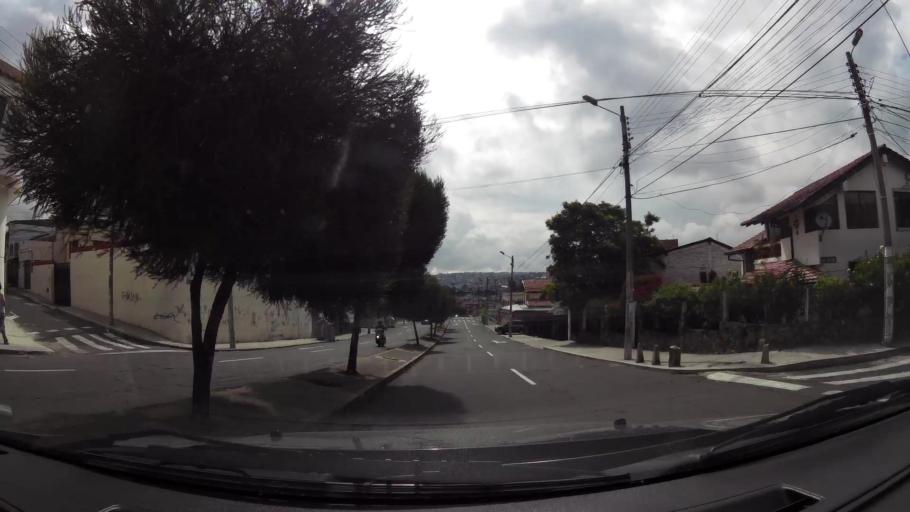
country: EC
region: Pichincha
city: Quito
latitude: -0.1446
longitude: -78.4983
